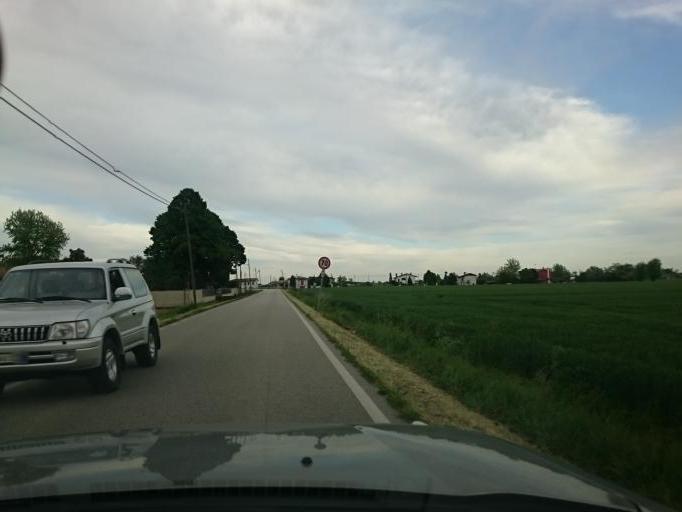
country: IT
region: Veneto
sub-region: Provincia di Padova
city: Pernumia
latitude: 45.2395
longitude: 11.7916
